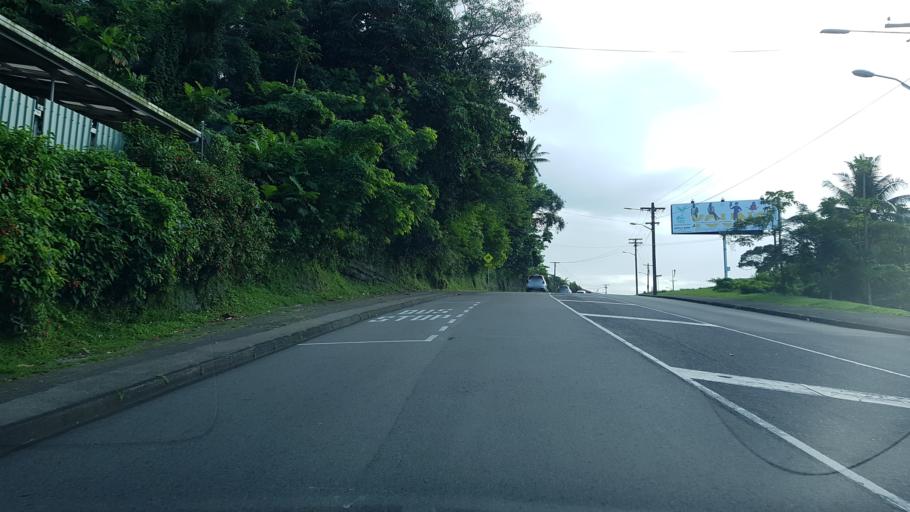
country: FJ
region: Central
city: Suva
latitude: -18.1457
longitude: 178.4398
